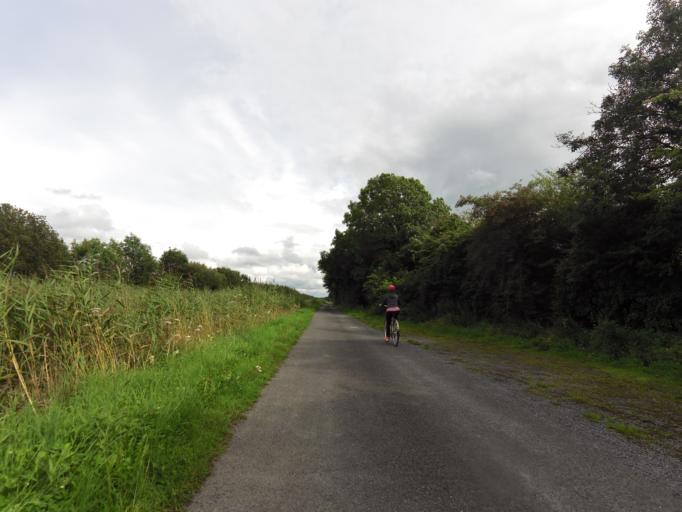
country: IE
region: Leinster
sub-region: An Longfort
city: Edgeworthstown
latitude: 53.5693
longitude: -7.5161
